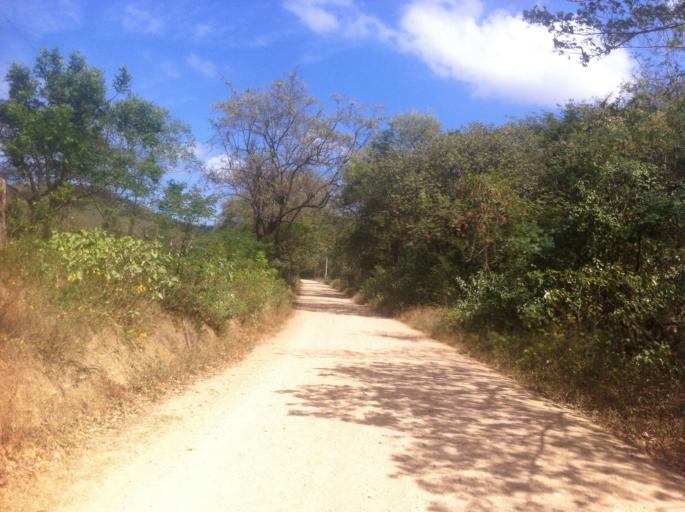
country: NI
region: Rivas
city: Tola
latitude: 11.3963
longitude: -86.0303
